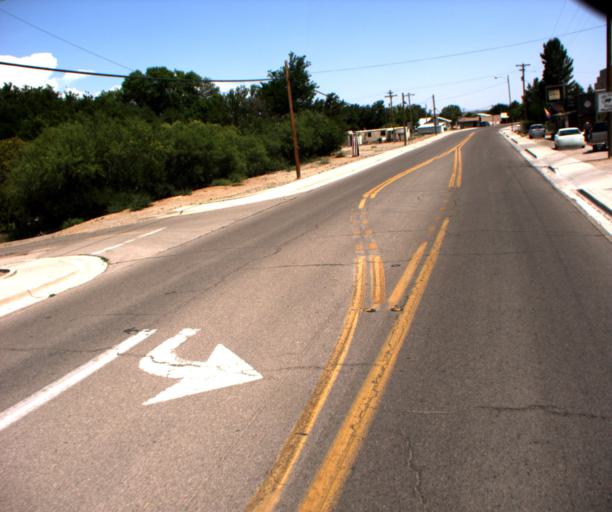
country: US
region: Arizona
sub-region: Greenlee County
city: Clifton
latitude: 32.7170
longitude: -109.1025
